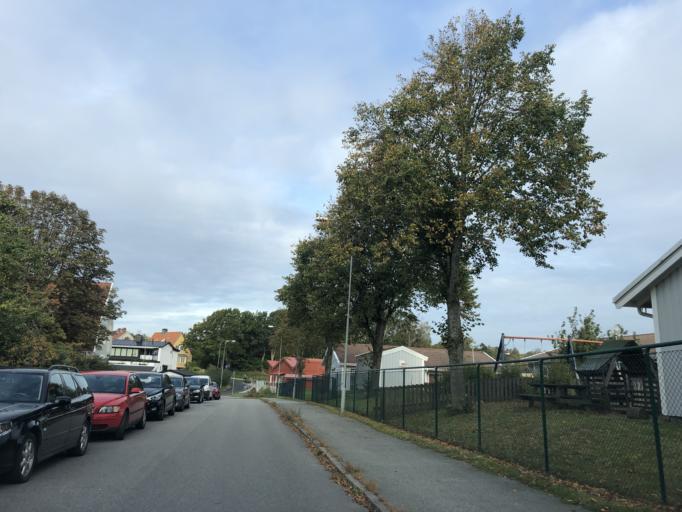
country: SE
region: Vaestra Goetaland
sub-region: Goteborg
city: Majorna
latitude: 57.6692
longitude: 11.8797
